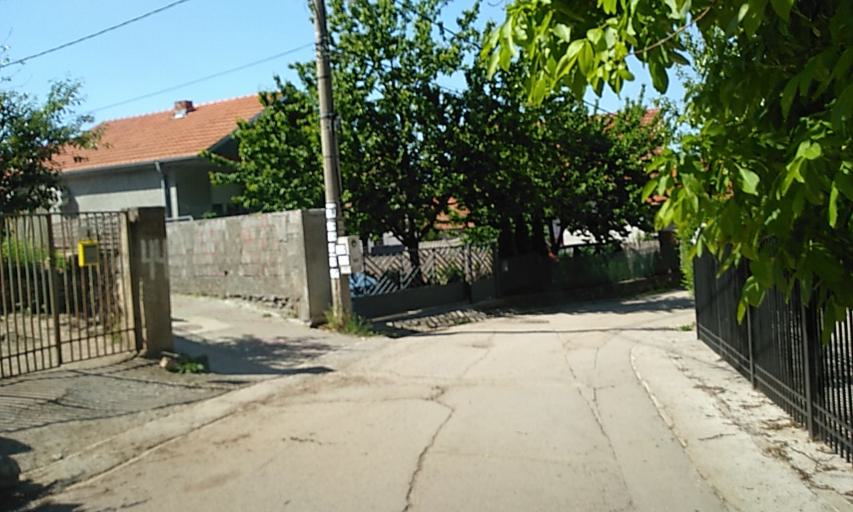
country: RS
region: Central Serbia
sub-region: Nisavski Okrug
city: Niska Banja
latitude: 43.2934
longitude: 22.0149
